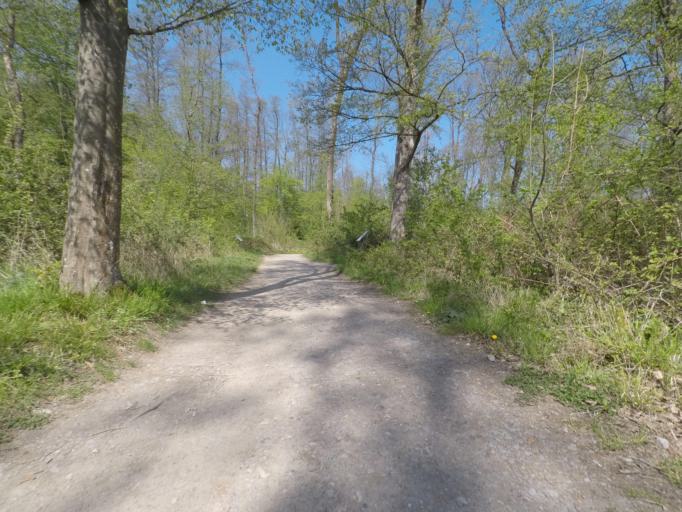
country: AT
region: Lower Austria
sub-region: Politischer Bezirk Modling
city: Perchtoldsdorf
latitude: 48.1702
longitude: 16.2490
